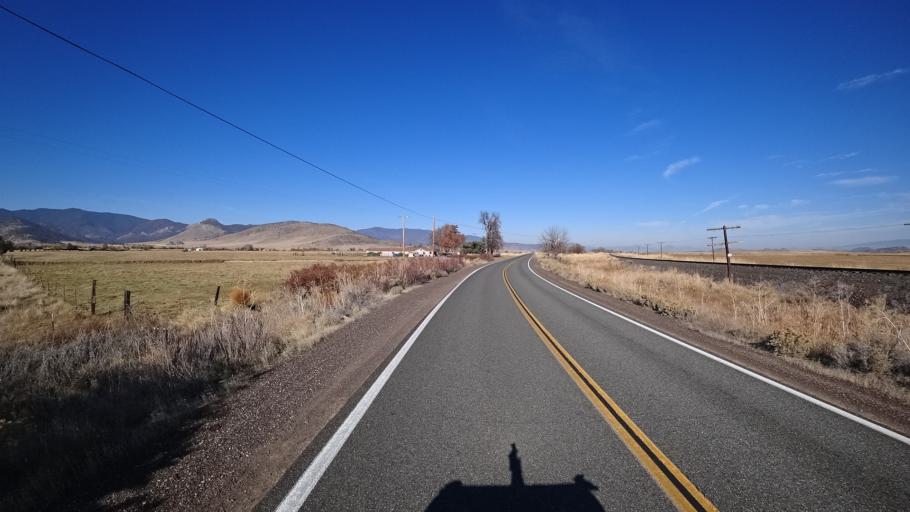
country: US
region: California
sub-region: Siskiyou County
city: Weed
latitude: 41.4967
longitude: -122.5123
